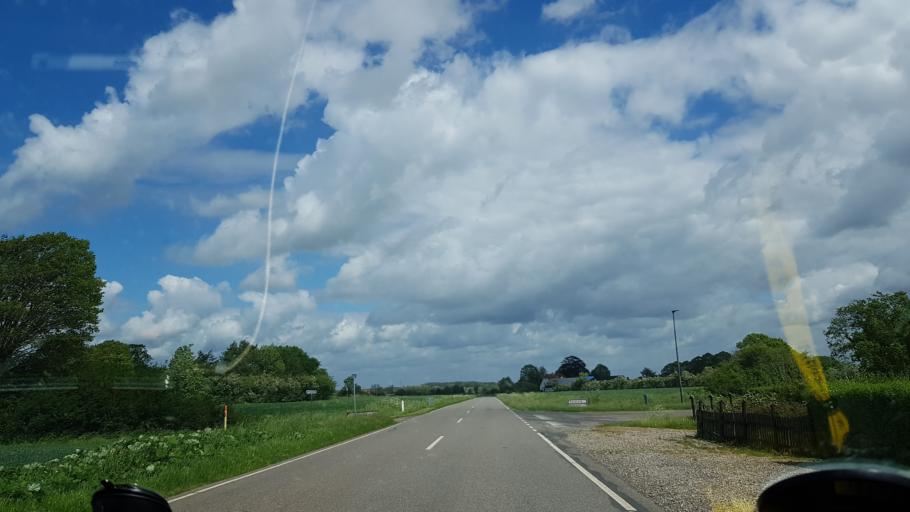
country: DK
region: South Denmark
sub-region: Kolding Kommune
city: Christiansfeld
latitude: 55.3401
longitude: 9.4643
